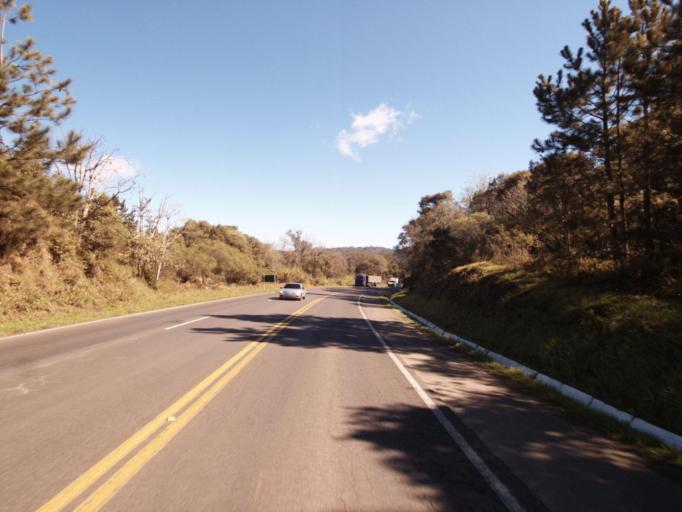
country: BR
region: Santa Catarina
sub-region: Joacaba
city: Joacaba
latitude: -27.1715
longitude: -51.5574
